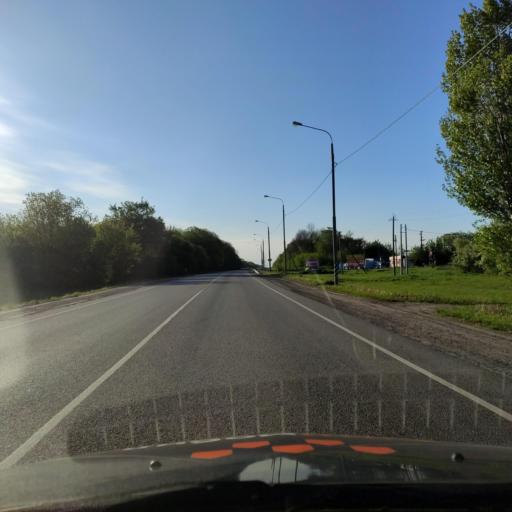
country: RU
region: Lipetsk
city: Yelets
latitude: 52.5809
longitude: 38.6344
